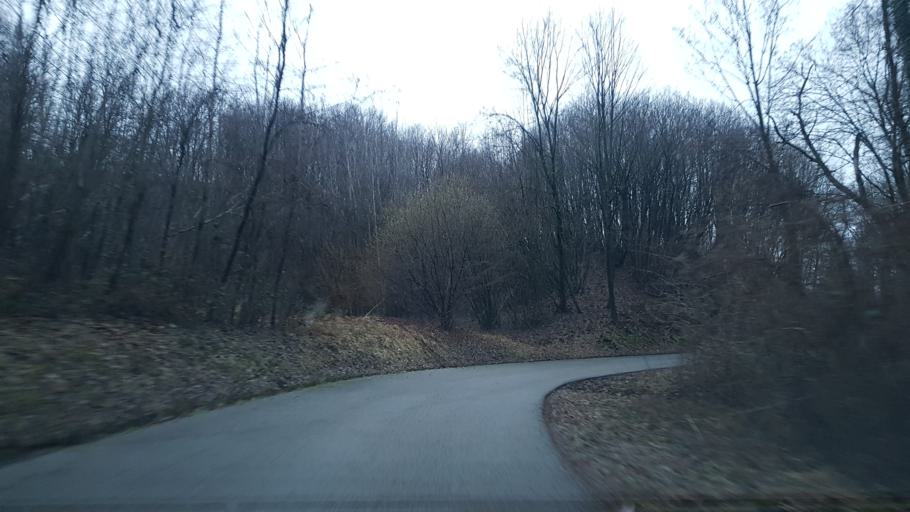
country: IT
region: Friuli Venezia Giulia
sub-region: Provincia di Udine
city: Stregna
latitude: 46.1042
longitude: 13.5607
